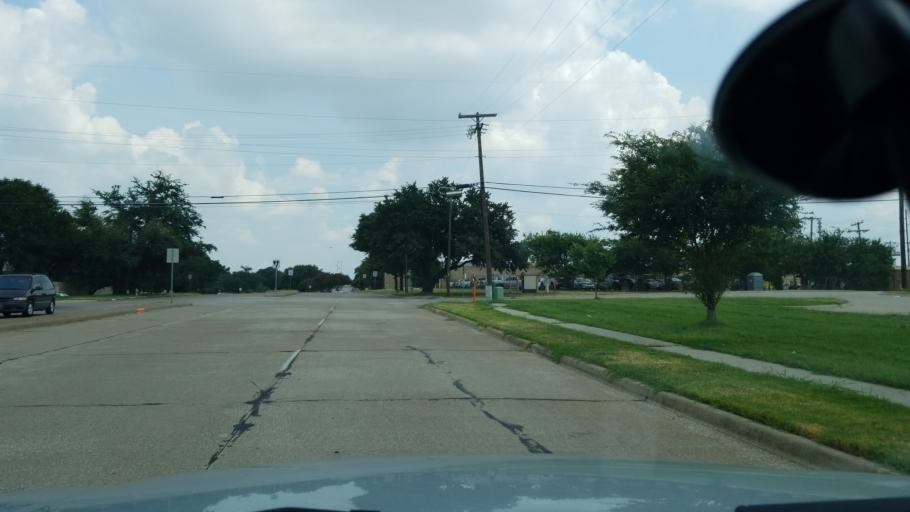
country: US
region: Texas
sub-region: Dallas County
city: Irving
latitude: 32.8364
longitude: -96.8932
